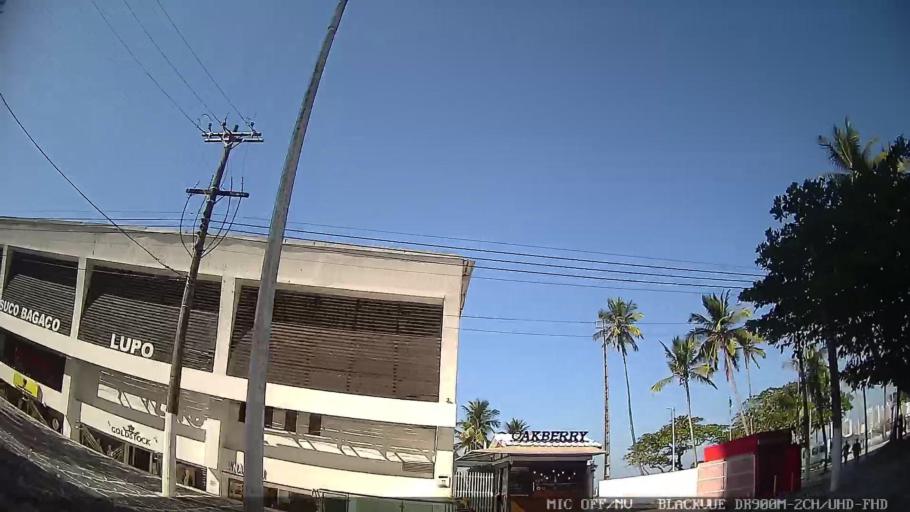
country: BR
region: Sao Paulo
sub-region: Guaruja
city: Guaruja
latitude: -23.9975
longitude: -46.2576
